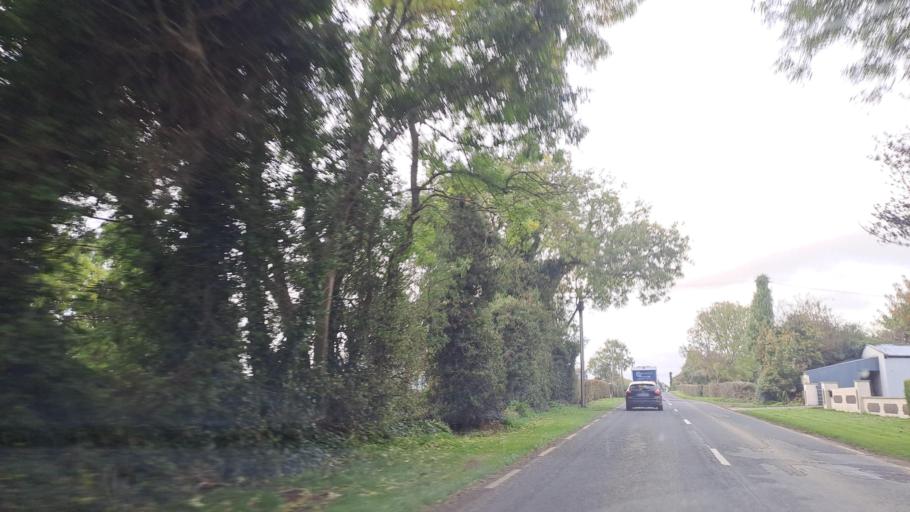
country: IE
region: Leinster
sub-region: An Mhi
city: Navan
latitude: 53.7197
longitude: -6.6992
